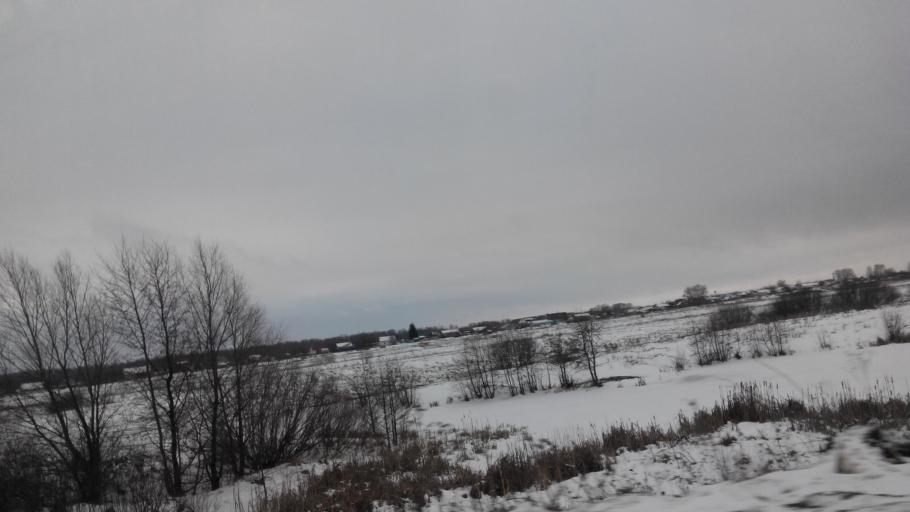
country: RU
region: Tula
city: Mayskiy
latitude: 53.9725
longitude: 38.2465
